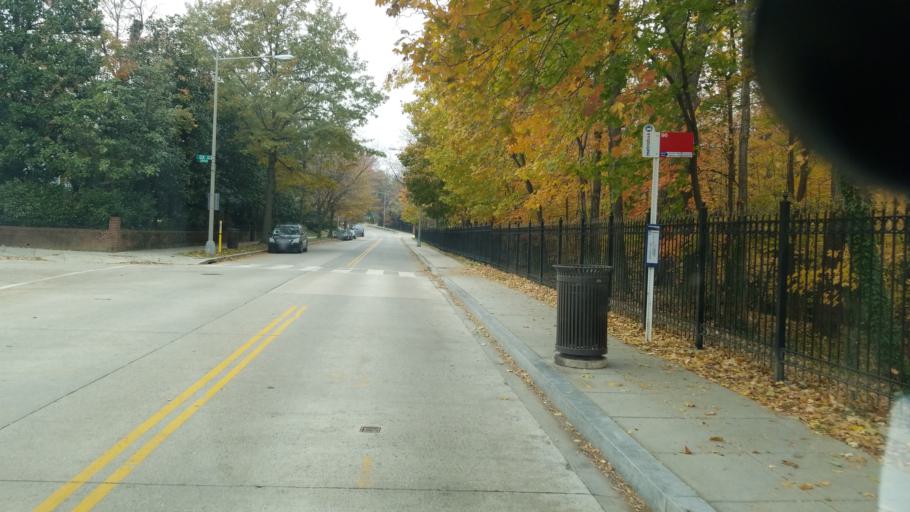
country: US
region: Maryland
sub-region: Montgomery County
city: Friendship Village
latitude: 38.9305
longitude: -77.0629
